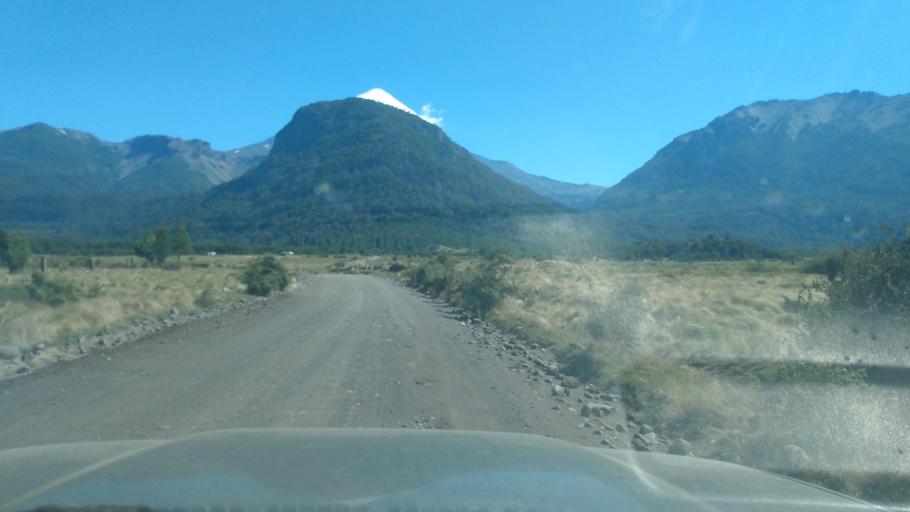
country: AR
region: Neuquen
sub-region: Departamento de Lacar
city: San Martin de los Andes
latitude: -39.7414
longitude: -71.5217
